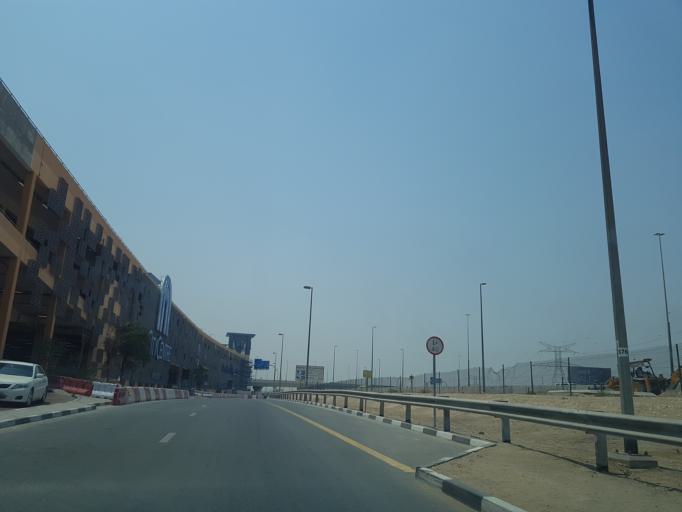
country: AE
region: Ash Shariqah
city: Sharjah
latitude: 25.2192
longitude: 55.4058
